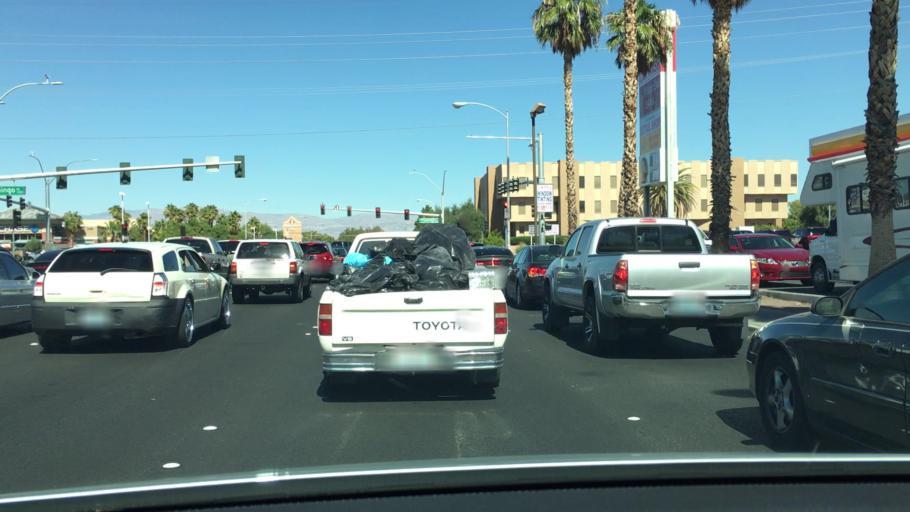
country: US
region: Nevada
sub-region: Clark County
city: Winchester
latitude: 36.1145
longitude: -115.1008
